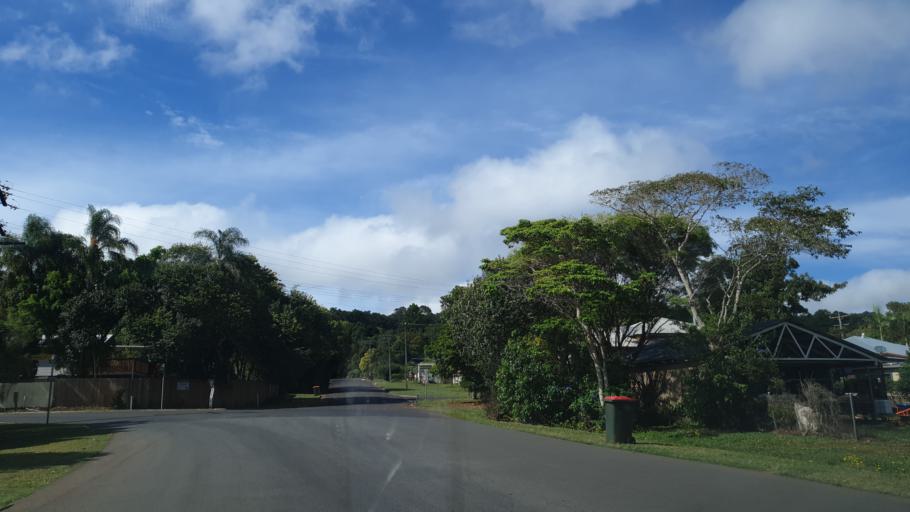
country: AU
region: Queensland
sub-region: Tablelands
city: Atherton
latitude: -17.3524
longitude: 145.5913
